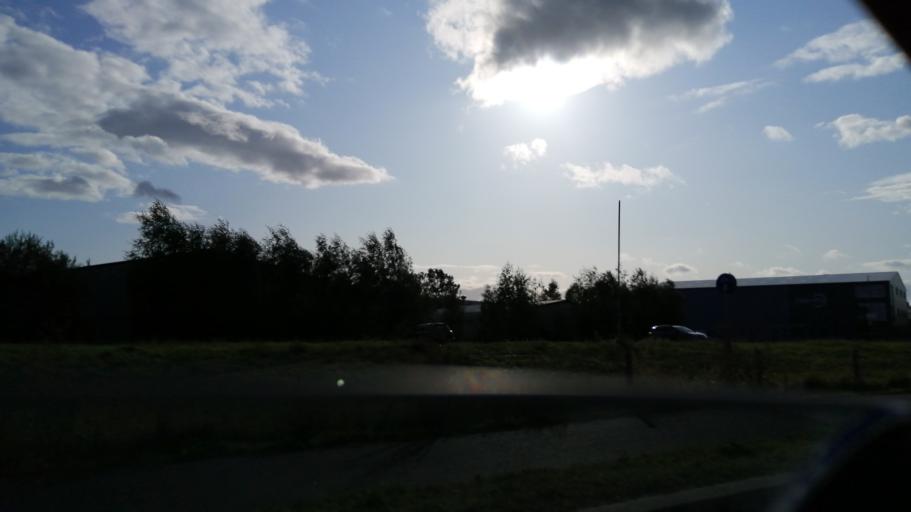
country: GB
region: England
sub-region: Herefordshire
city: Lower Bullingham
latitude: 52.0410
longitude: -2.6875
